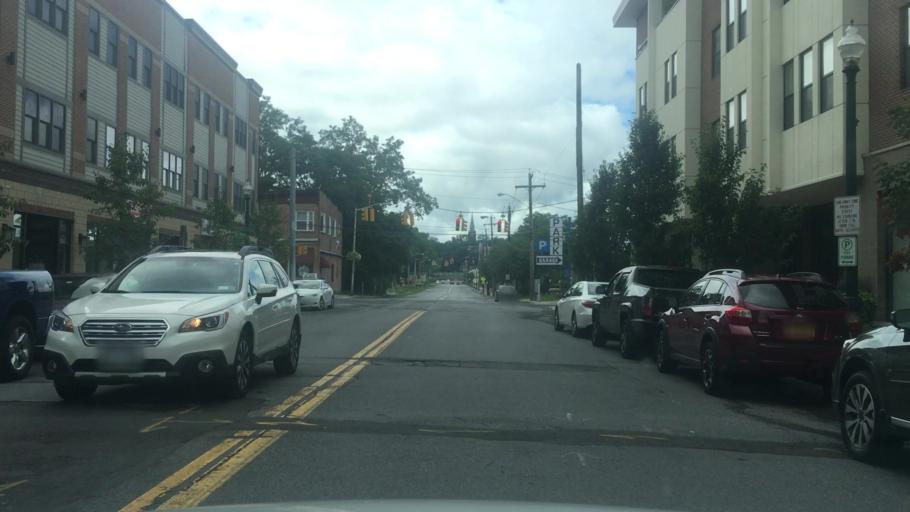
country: US
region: New York
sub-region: Schenectady County
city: Schenectady
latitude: 42.8114
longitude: -73.9438
